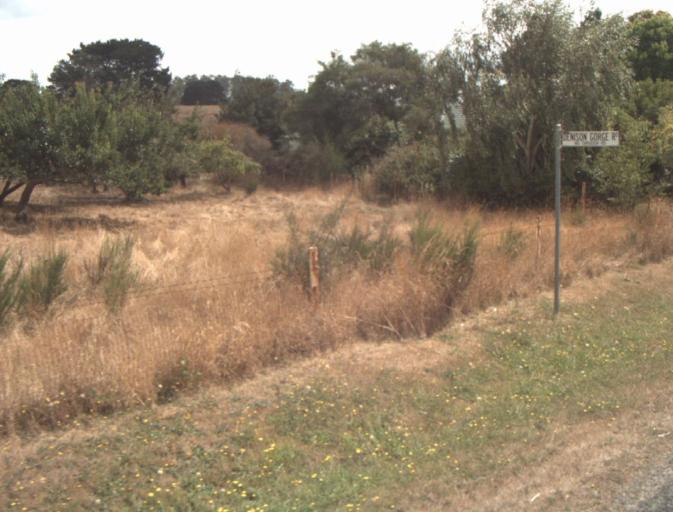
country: AU
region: Tasmania
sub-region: Launceston
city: Mayfield
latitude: -41.1975
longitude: 147.2189
